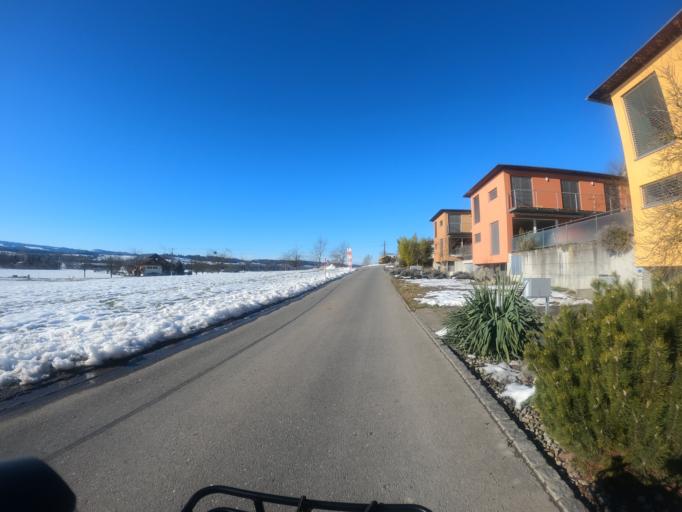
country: CH
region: Aargau
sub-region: Bezirk Bremgarten
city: Jonen
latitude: 47.2976
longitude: 8.3907
